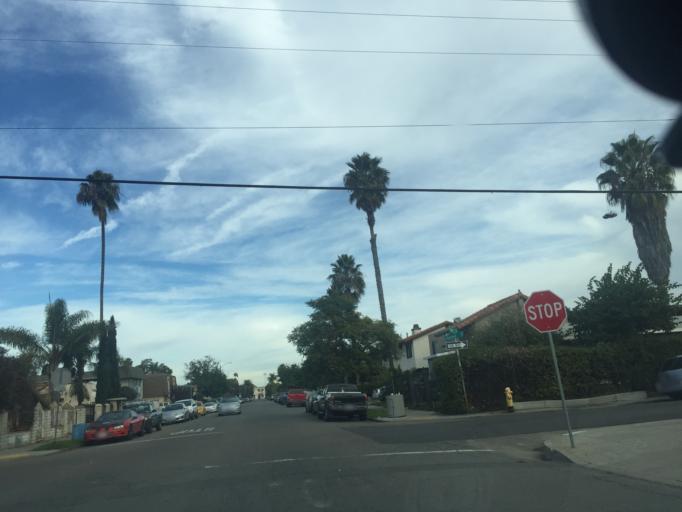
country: US
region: California
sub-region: San Diego County
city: Lemon Grove
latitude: 32.7512
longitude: -117.0987
